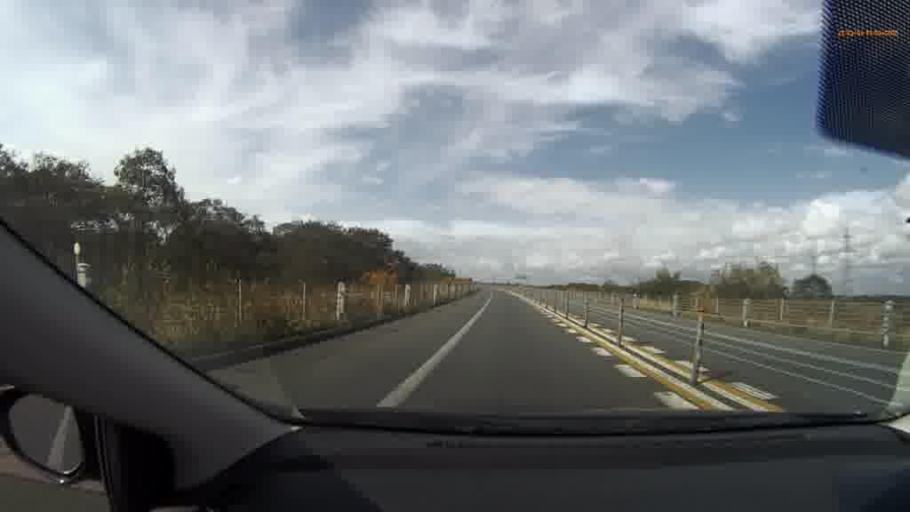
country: JP
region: Hokkaido
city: Kushiro
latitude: 43.0319
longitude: 144.3969
